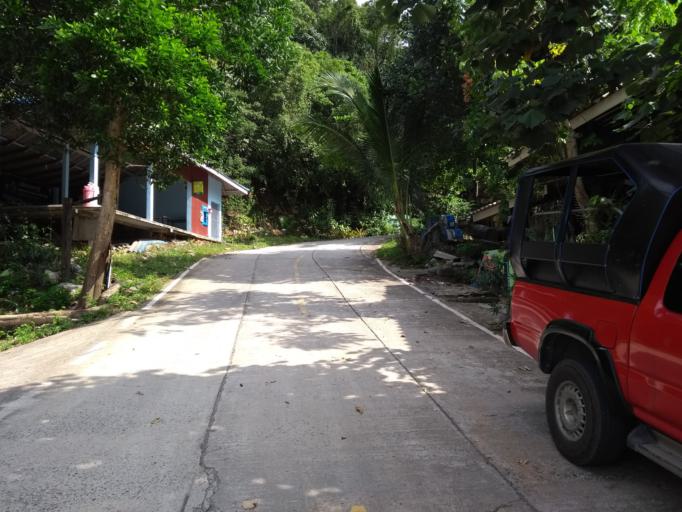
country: TH
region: Trat
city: Ko Kut
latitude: 11.6082
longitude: 102.5946
